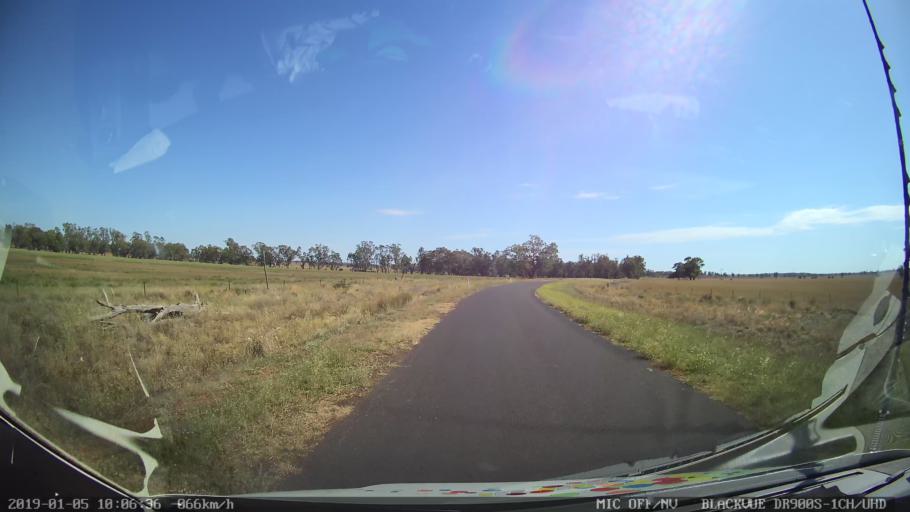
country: AU
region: New South Wales
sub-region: Gilgandra
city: Gilgandra
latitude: -31.6567
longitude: 148.8700
